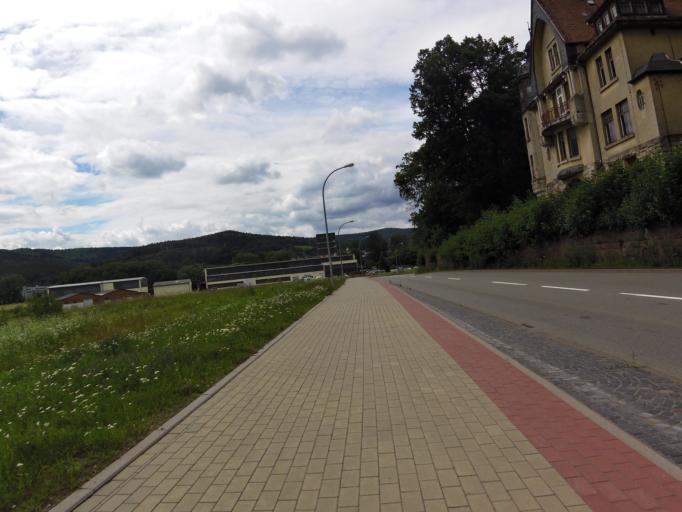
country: DE
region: Thuringia
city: Fambach
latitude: 50.7185
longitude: 10.3652
